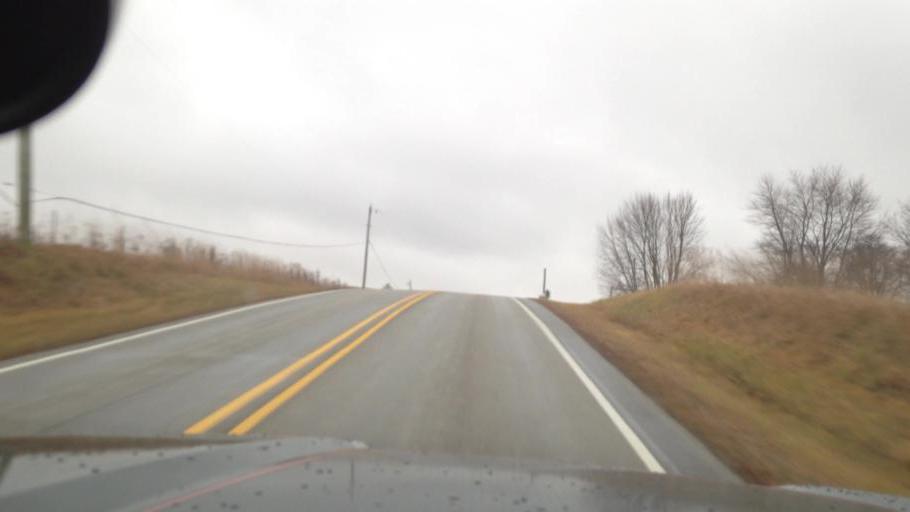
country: US
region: Ohio
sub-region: Preble County
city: New Paris
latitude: 39.9094
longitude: -84.8317
